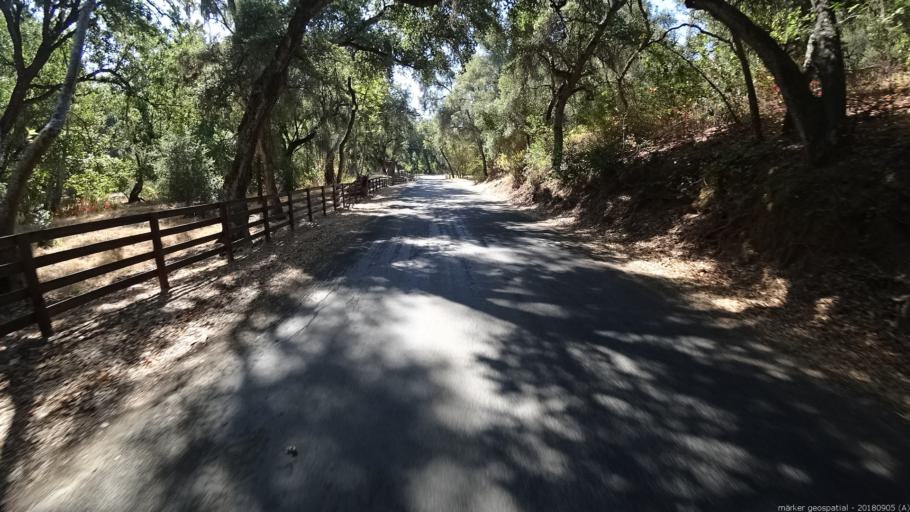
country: US
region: California
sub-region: Monterey County
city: Gonzales
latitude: 36.3779
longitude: -121.5923
